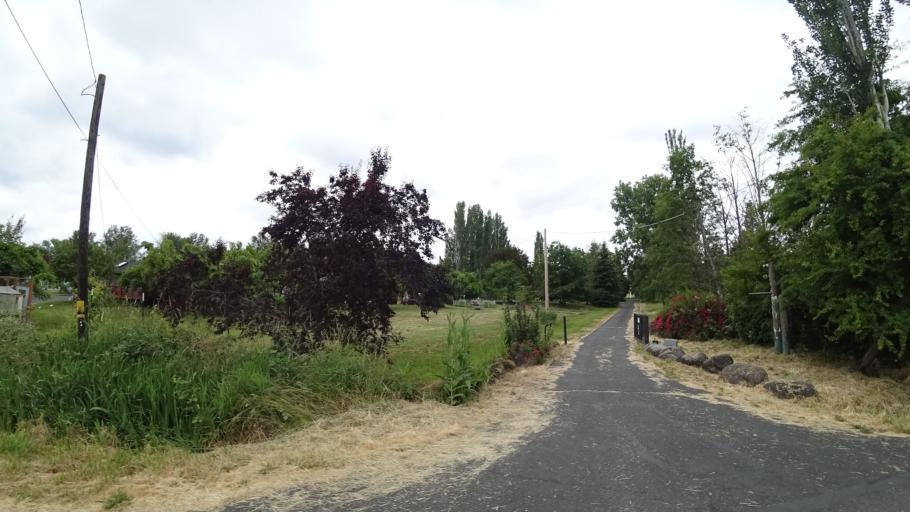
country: US
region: Washington
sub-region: Clark County
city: Vancouver
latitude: 45.5936
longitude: -122.6520
